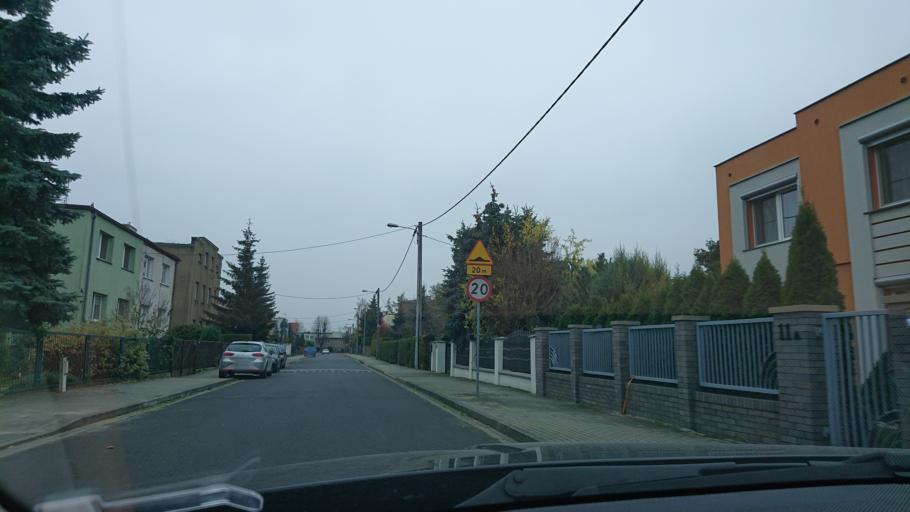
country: PL
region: Greater Poland Voivodeship
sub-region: Powiat gnieznienski
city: Gniezno
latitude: 52.5348
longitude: 17.6238
